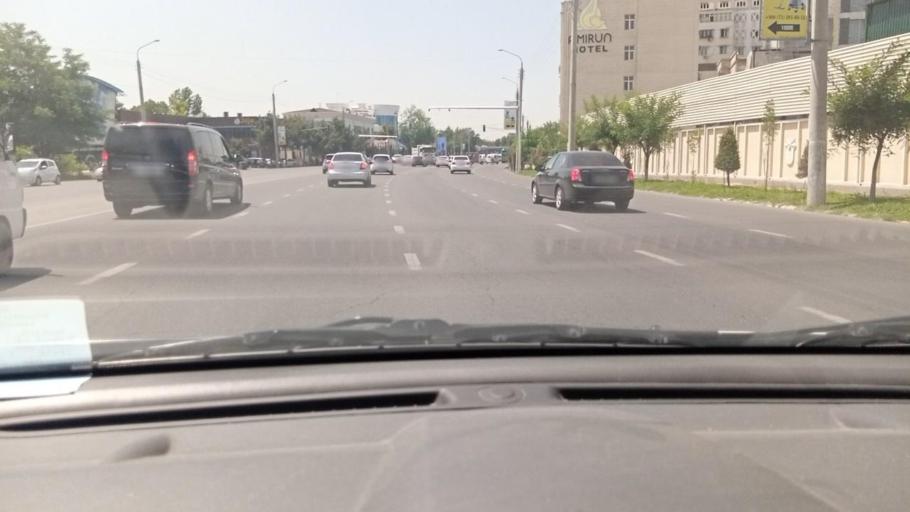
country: UZ
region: Toshkent Shahri
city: Tashkent
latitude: 41.2711
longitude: 69.2660
